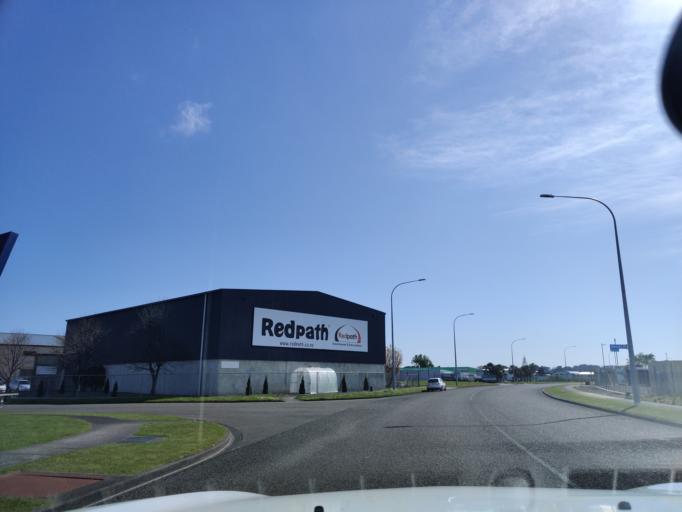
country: NZ
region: Manawatu-Wanganui
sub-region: Palmerston North City
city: Palmerston North
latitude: -40.3346
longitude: 175.6448
